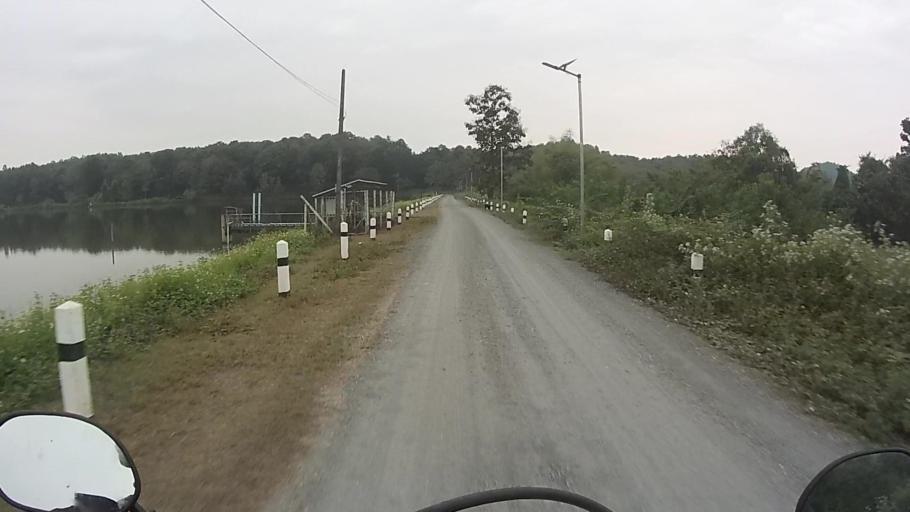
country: TH
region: Chiang Mai
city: Mae On
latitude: 18.8610
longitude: 99.2448
